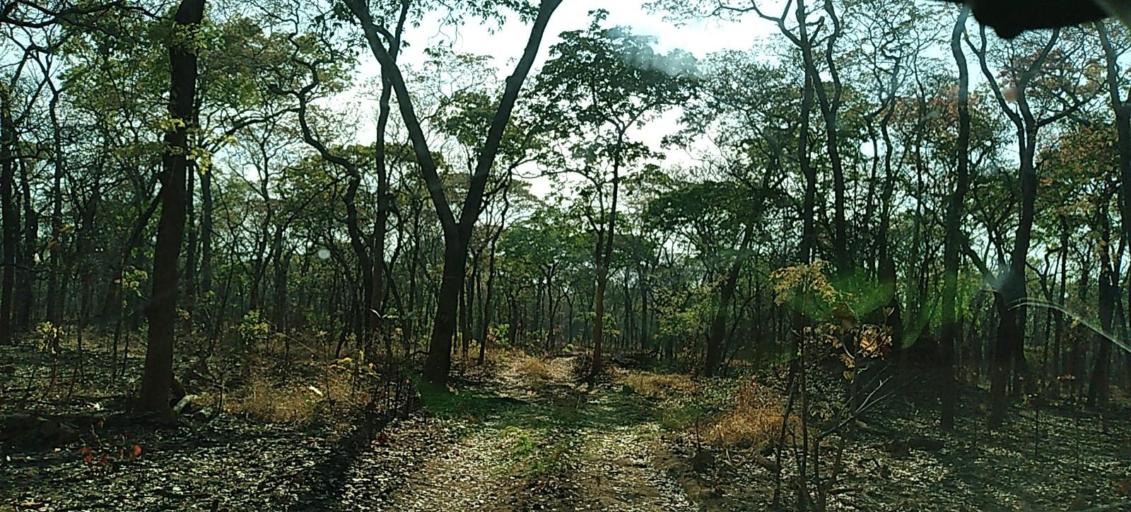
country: ZM
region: North-Western
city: Kalengwa
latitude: -13.2287
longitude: 25.0807
